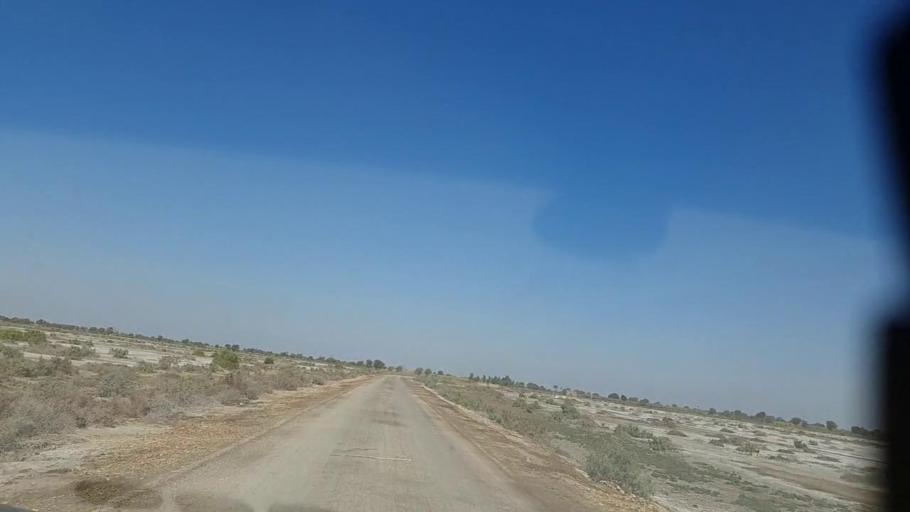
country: PK
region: Sindh
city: Digri
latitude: 25.1638
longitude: 69.0487
